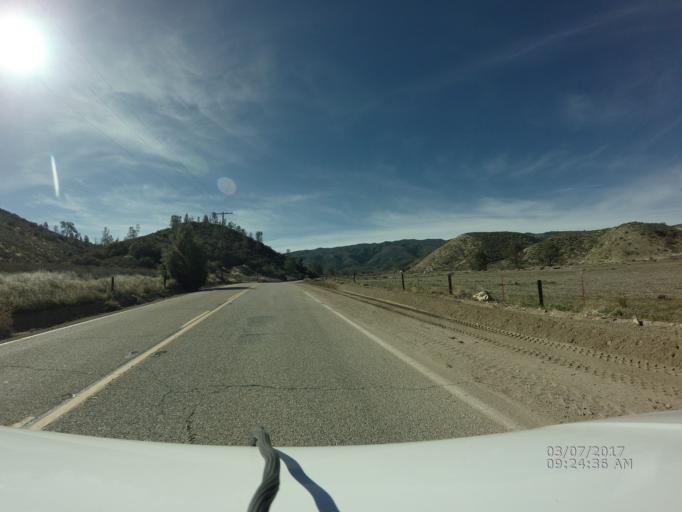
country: US
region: California
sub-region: Los Angeles County
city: Green Valley
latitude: 34.7553
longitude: -118.5989
